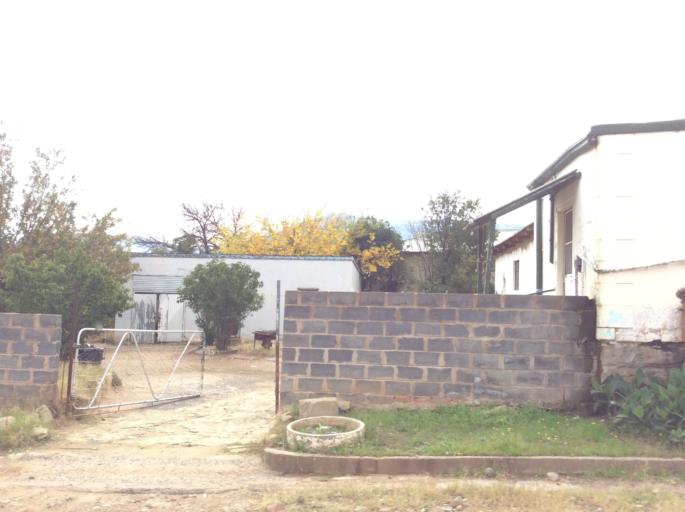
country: LS
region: Mafeteng
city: Mafeteng
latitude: -29.7306
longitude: 27.0428
